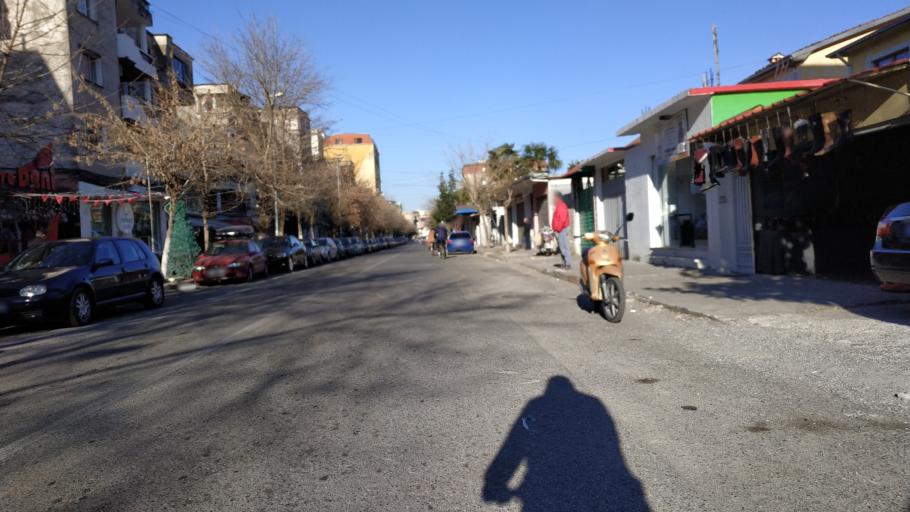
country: AL
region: Shkoder
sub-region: Rrethi i Shkodres
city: Shkoder
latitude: 42.0624
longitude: 19.5114
